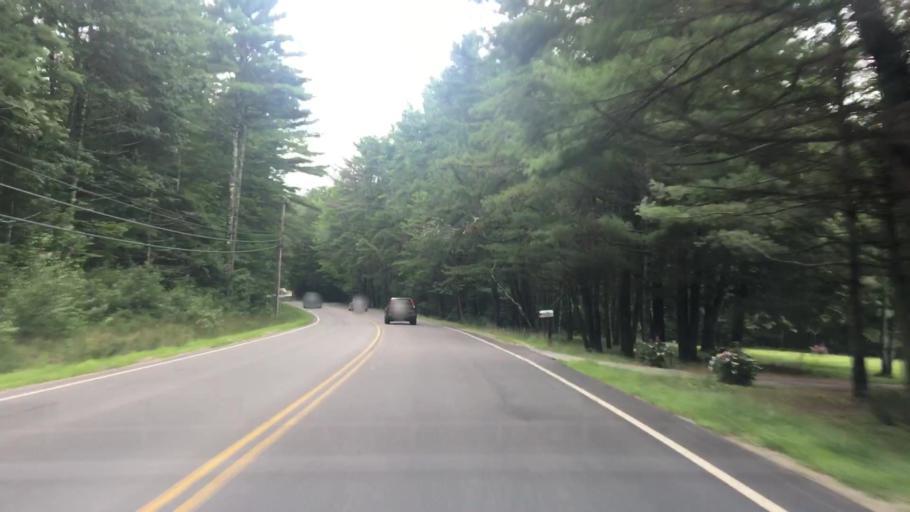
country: US
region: Maine
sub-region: York County
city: Dayton
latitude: 43.5254
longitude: -70.5852
